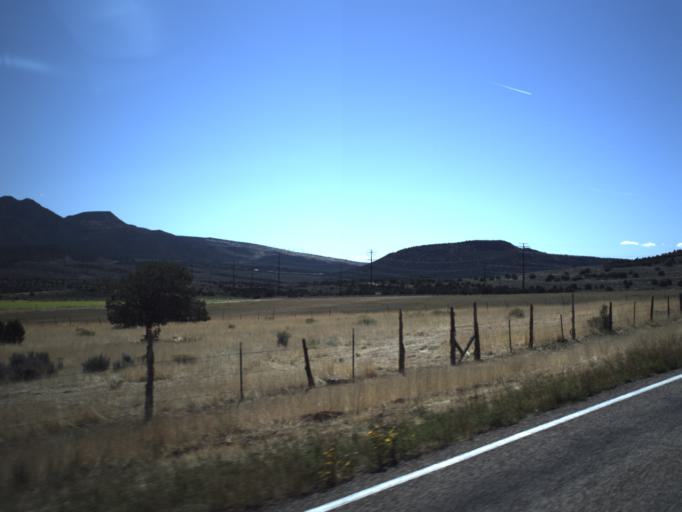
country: US
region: Utah
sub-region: Washington County
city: Enterprise
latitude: 37.4077
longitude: -113.6351
